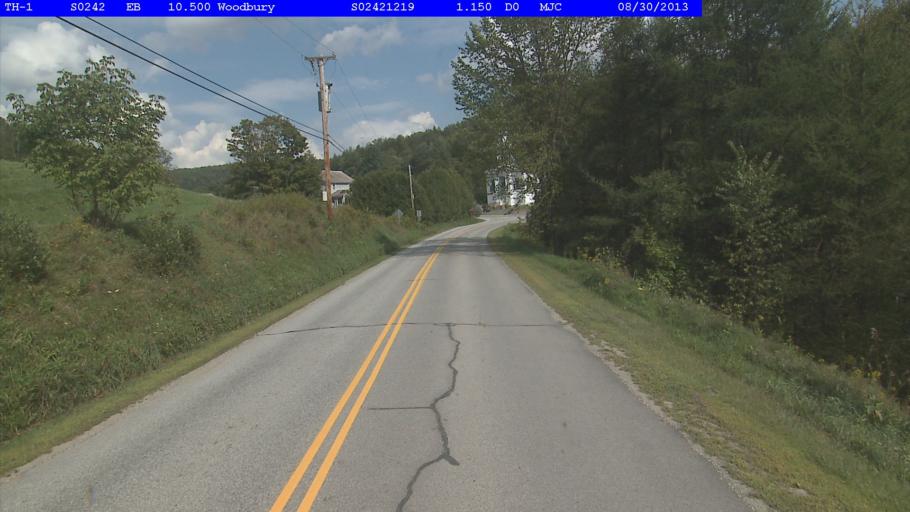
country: US
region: Vermont
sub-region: Caledonia County
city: Hardwick
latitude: 44.4151
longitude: -72.4193
